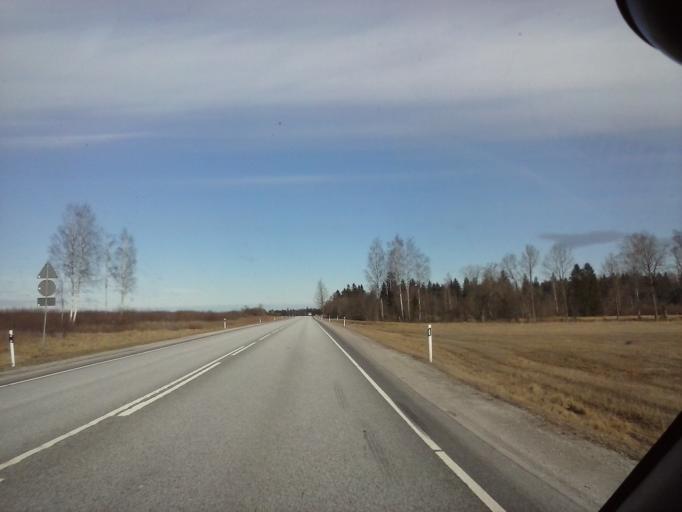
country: EE
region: Jaervamaa
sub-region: Paide linn
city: Paide
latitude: 59.0126
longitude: 25.5916
